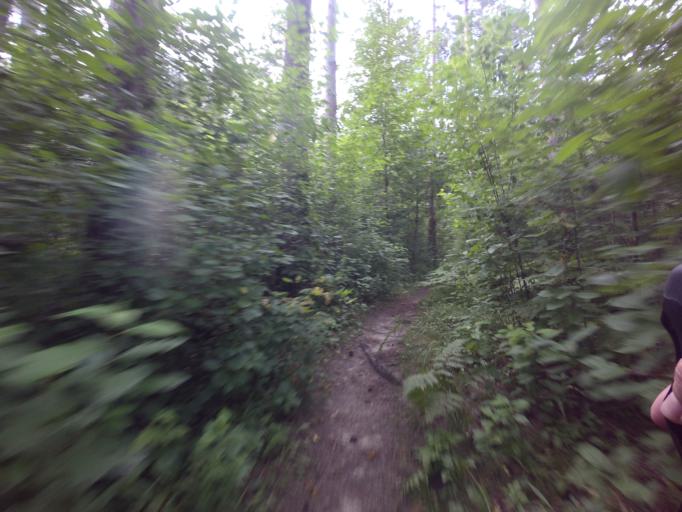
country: CA
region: Ontario
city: Bells Corners
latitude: 45.0307
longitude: -75.6601
